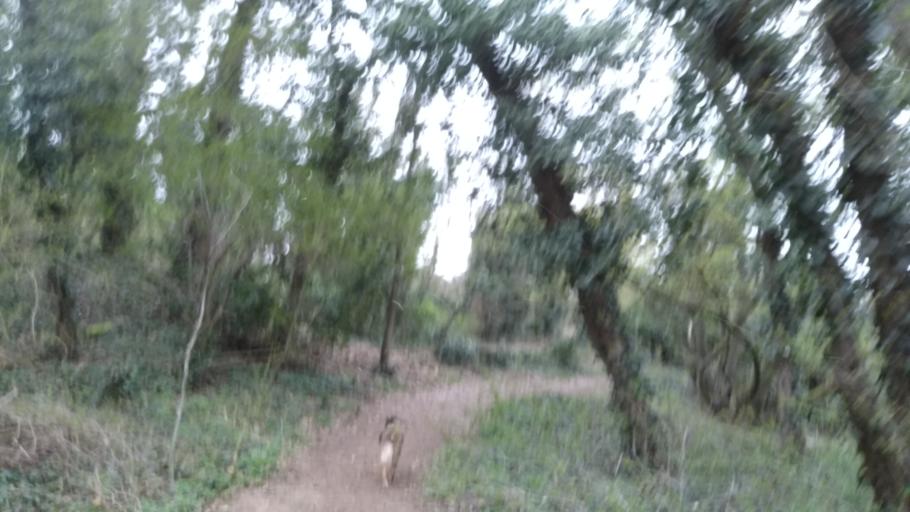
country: DE
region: Hesse
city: Pfungstadt
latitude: 49.8124
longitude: 8.6405
